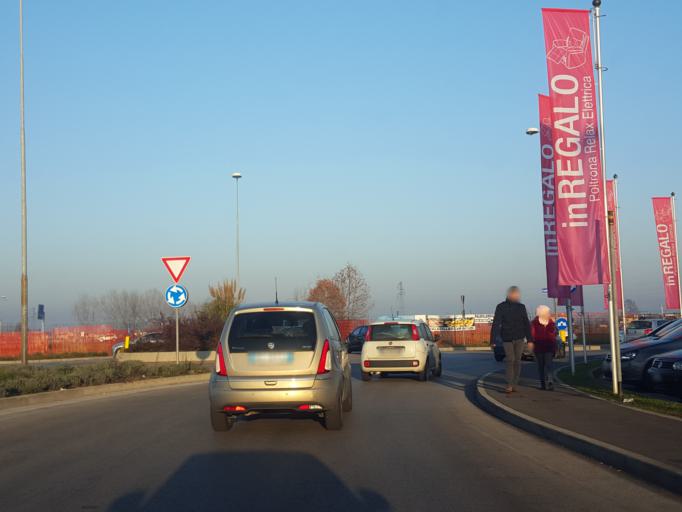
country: IT
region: Veneto
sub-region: Provincia di Vicenza
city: Torri di Quartesolo
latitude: 45.5094
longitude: 11.6278
